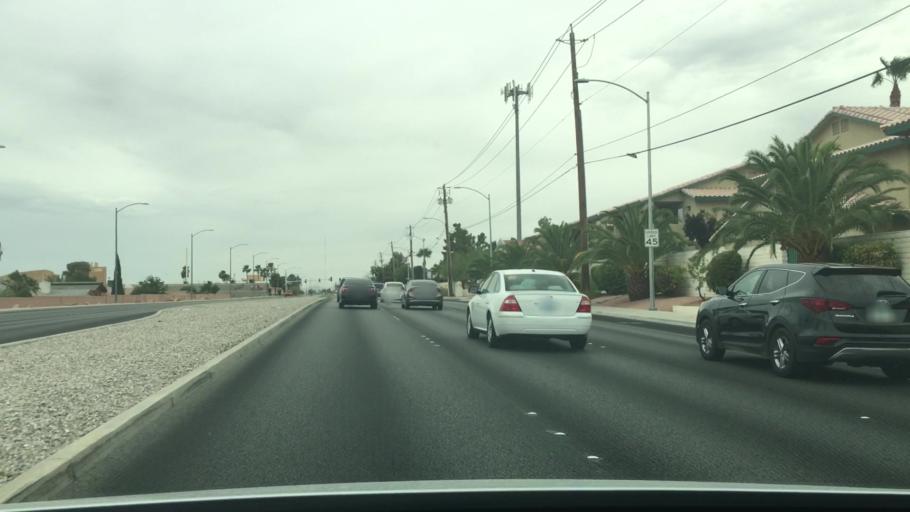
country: US
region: Nevada
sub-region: Clark County
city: Spring Valley
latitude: 36.1697
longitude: -115.2600
